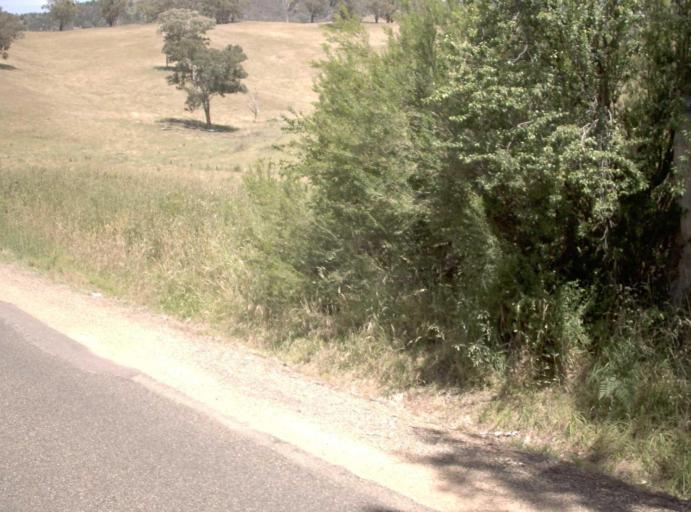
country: AU
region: Victoria
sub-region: East Gippsland
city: Bairnsdale
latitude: -37.4030
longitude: 147.8349
